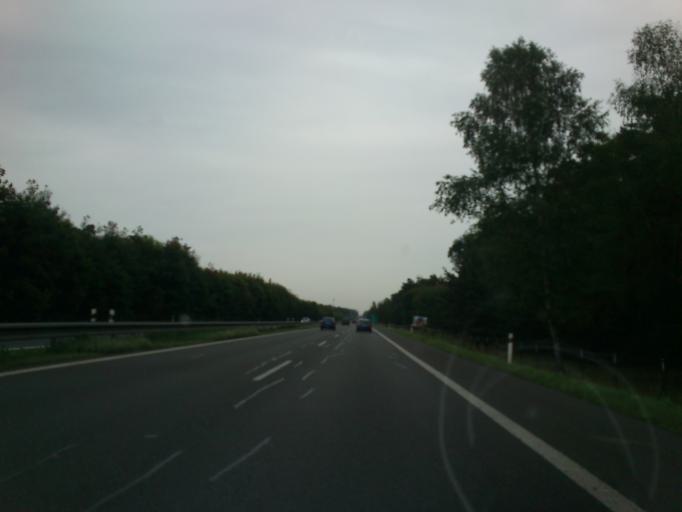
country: CZ
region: Central Bohemia
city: Brandys nad Labem-Stara Boleslav
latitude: 50.2183
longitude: 14.7098
